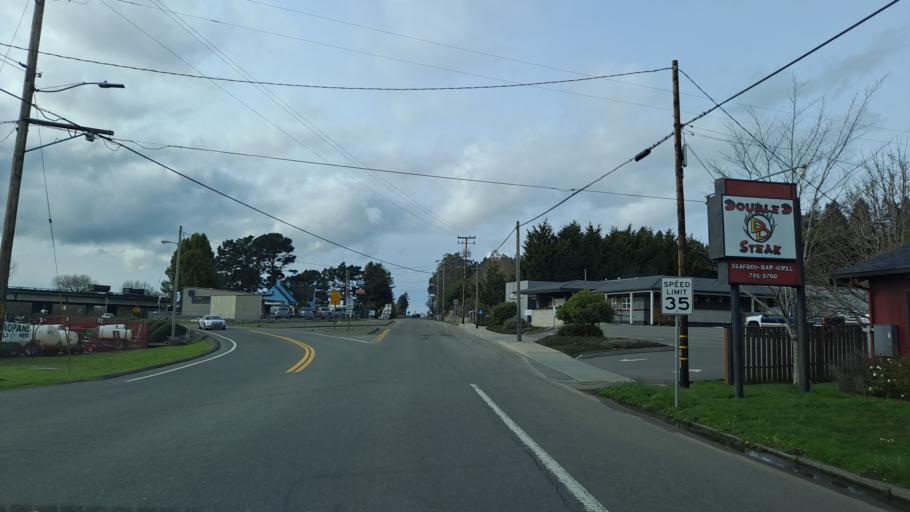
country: US
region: California
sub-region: Humboldt County
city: Fortuna
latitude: 40.5996
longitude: -124.1657
